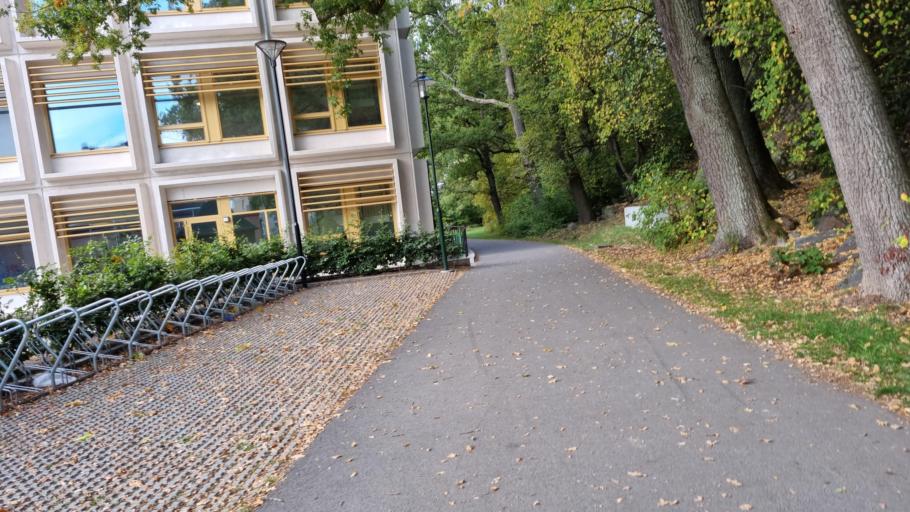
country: SE
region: Stockholm
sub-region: Huddinge Kommun
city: Huddinge
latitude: 59.2841
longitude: 17.9975
